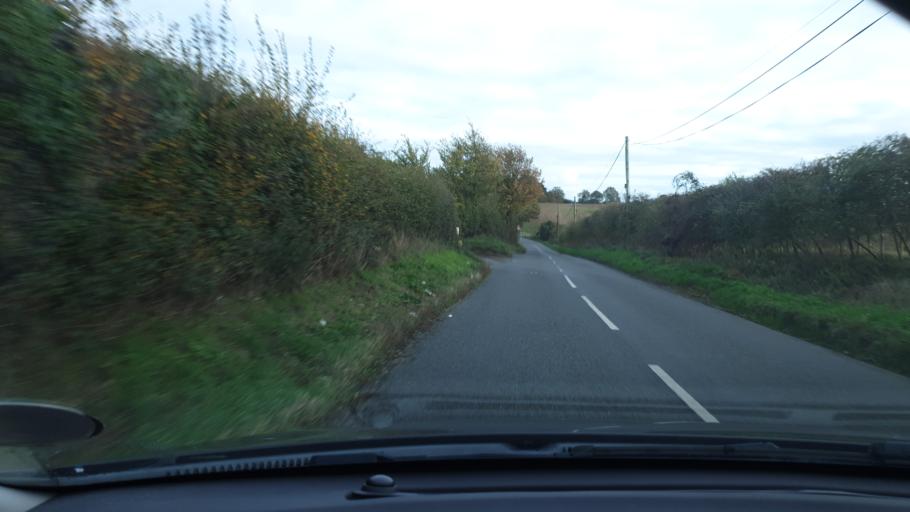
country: GB
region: England
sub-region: Essex
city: Mistley
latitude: 51.9256
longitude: 1.1212
